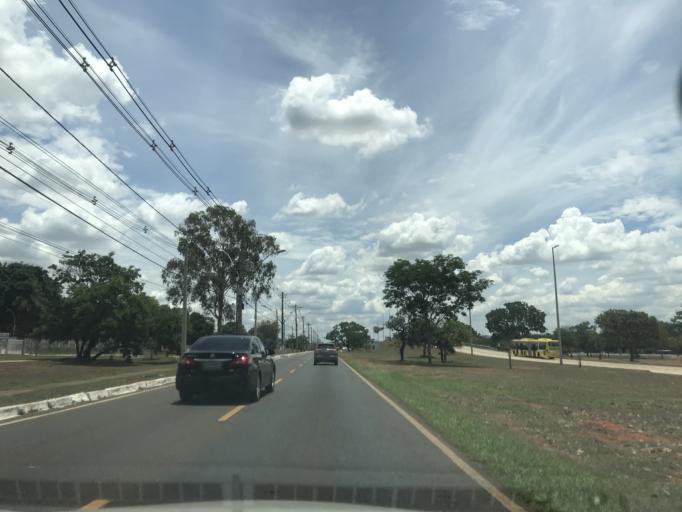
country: BR
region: Federal District
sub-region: Brasilia
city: Brasilia
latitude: -15.8693
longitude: -47.9453
